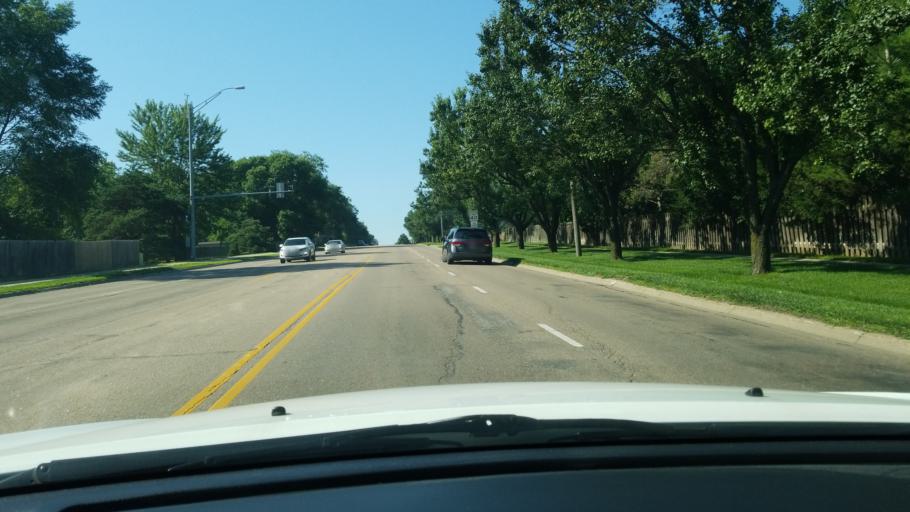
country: US
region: Nebraska
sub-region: Lancaster County
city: Lincoln
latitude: 40.8061
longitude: -96.6059
